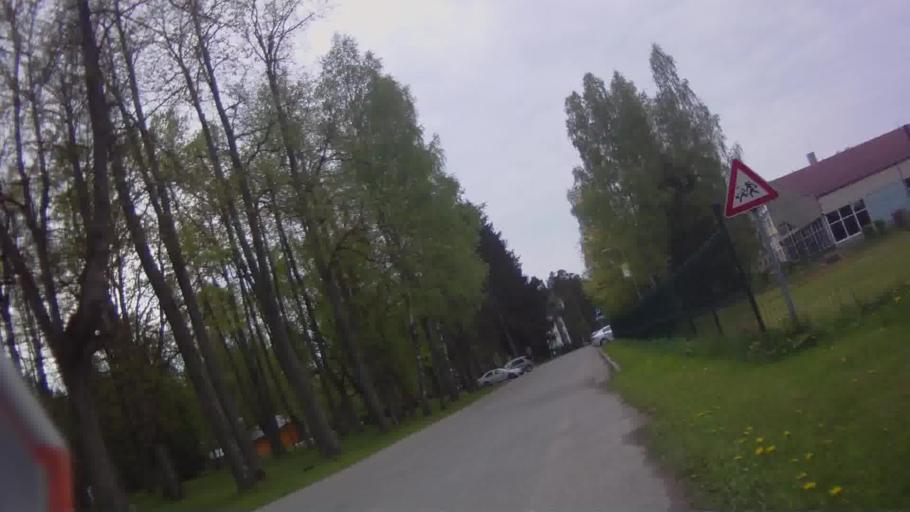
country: LV
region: Incukalns
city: Incukalns
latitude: 57.1008
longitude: 24.6844
